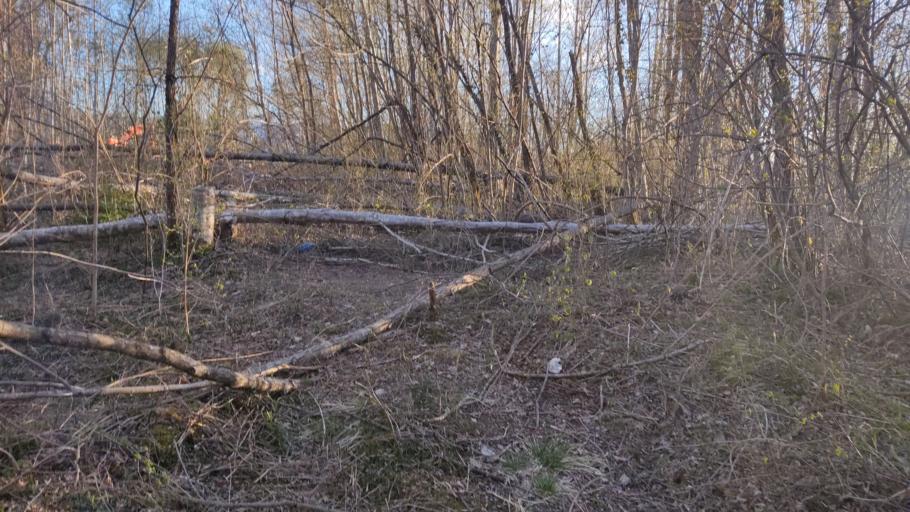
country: IT
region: Veneto
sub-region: Provincia di Belluno
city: Sedico
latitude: 46.0986
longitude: 12.0813
